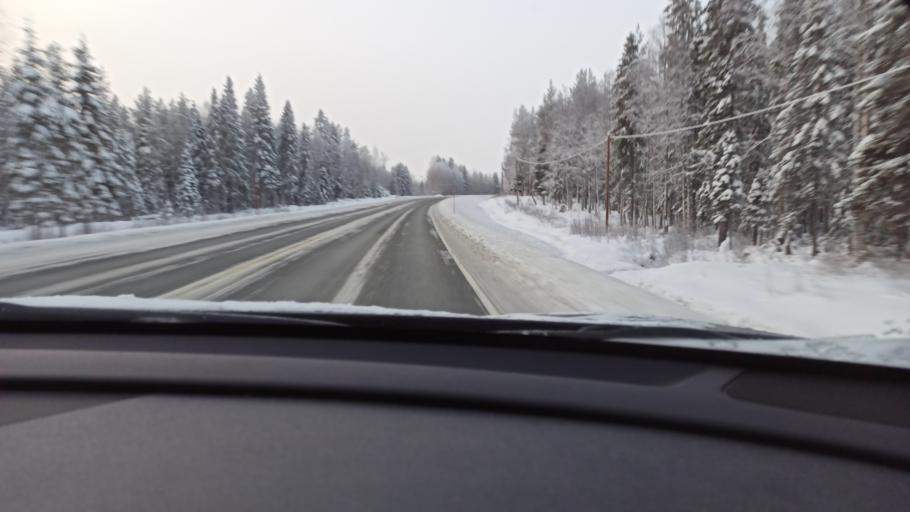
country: FI
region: Lapland
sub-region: Rovaniemi
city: Rovaniemi
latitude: 66.5523
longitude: 25.8952
